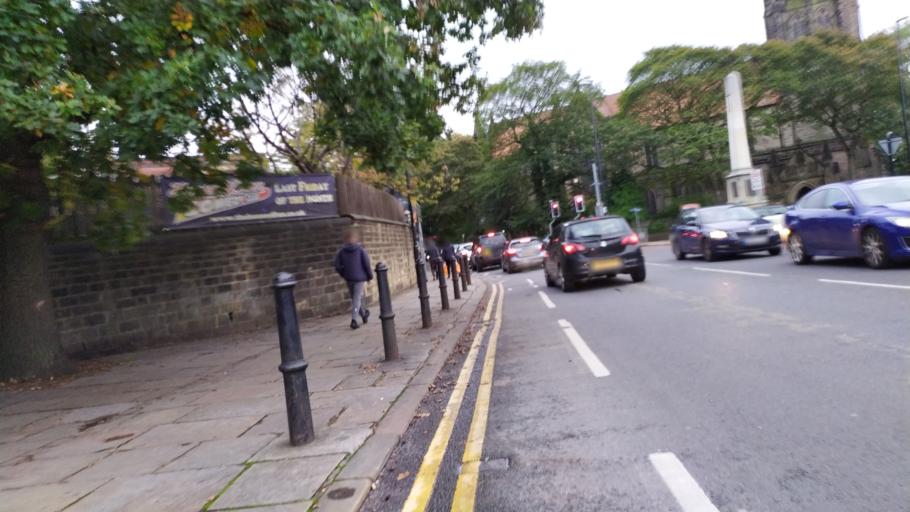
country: GB
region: England
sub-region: City and Borough of Leeds
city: Leeds
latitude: 53.8200
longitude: -1.5764
